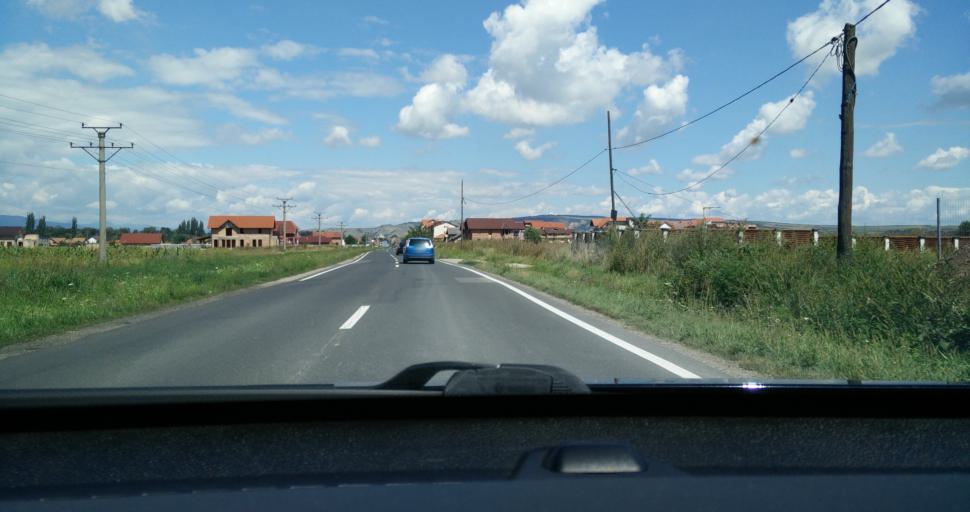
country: RO
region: Alba
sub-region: Municipiul Sebes
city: Petresti
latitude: 45.9334
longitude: 23.5612
